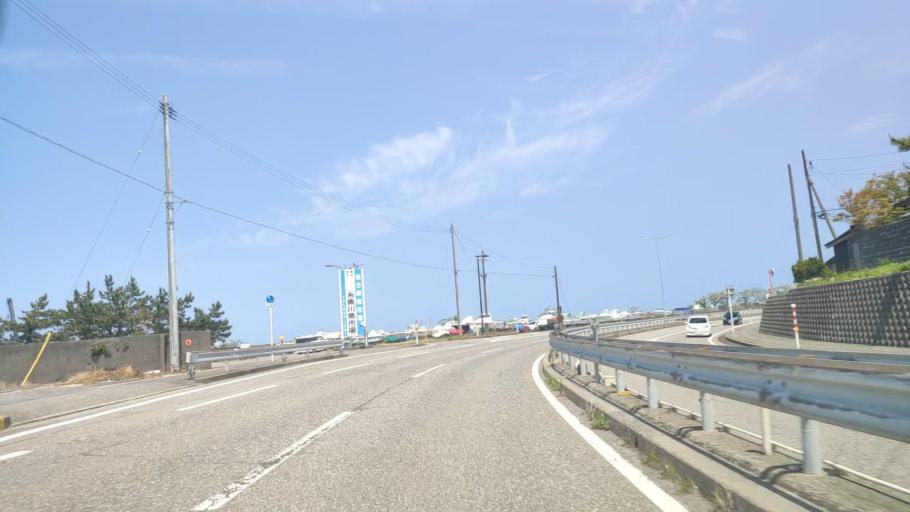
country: JP
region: Niigata
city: Itoigawa
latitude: 37.0431
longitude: 137.8463
